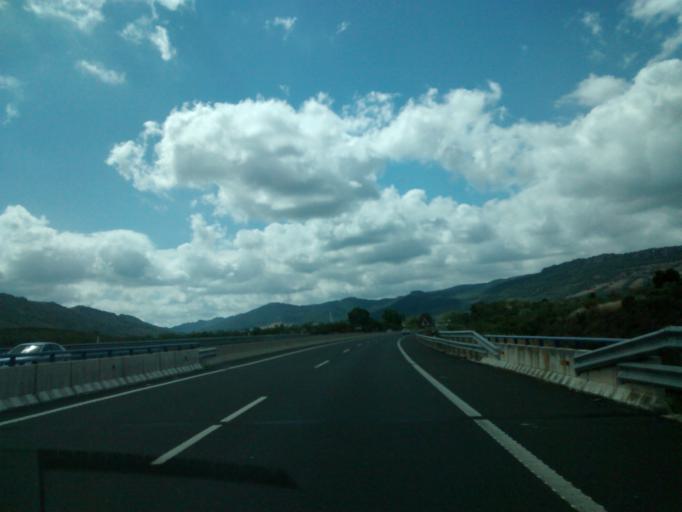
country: ES
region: Extremadura
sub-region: Provincia de Caceres
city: Romangordo
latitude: 39.7318
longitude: -5.7196
